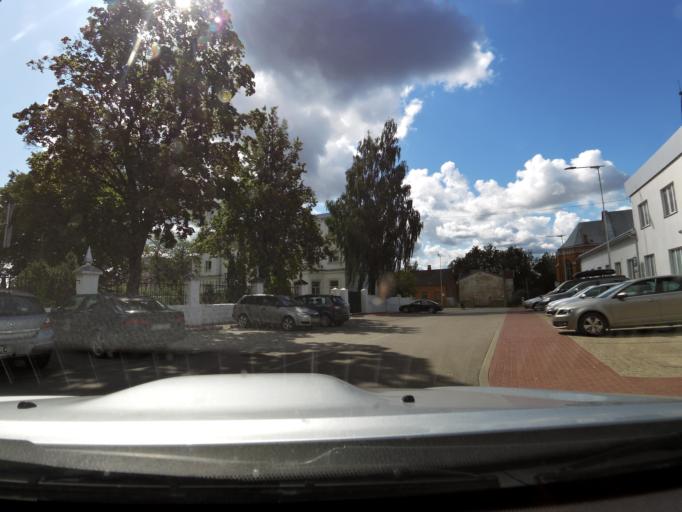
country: LV
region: Daugavpils
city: Daugavpils
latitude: 55.8711
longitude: 26.5423
